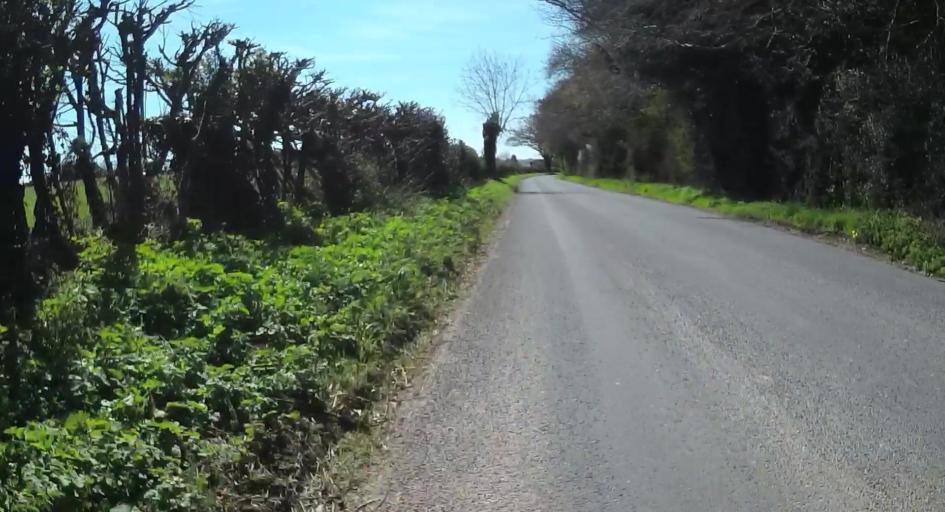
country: GB
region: England
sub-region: Hampshire
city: Winchester
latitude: 51.1024
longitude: -1.3954
